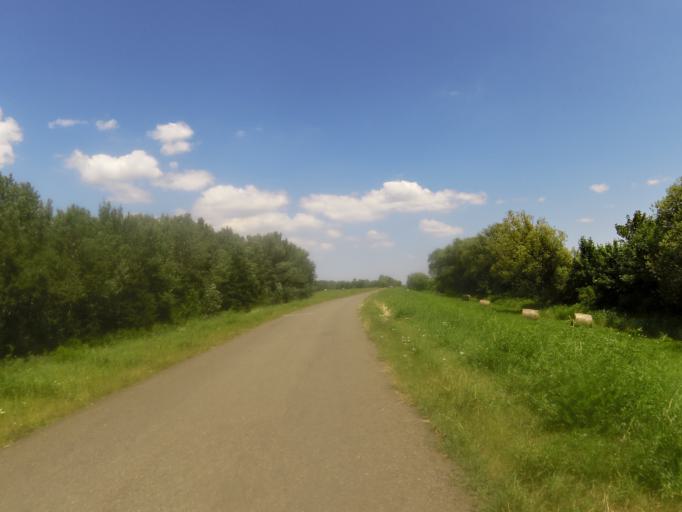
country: HU
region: Heves
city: Tiszanana
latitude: 47.5554
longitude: 20.6037
